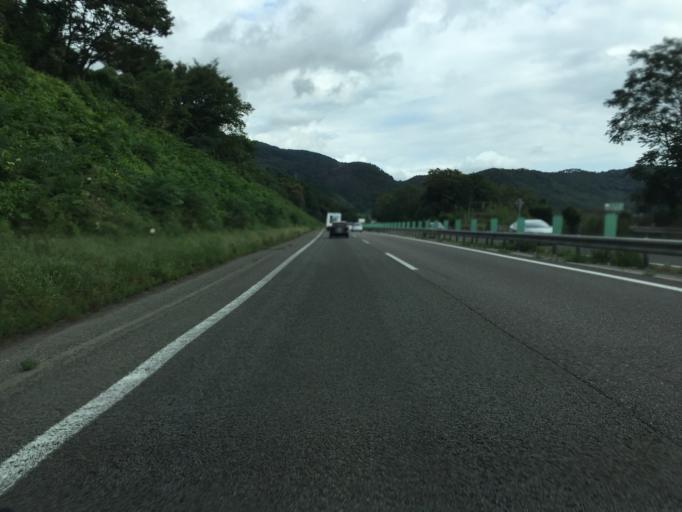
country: JP
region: Fukushima
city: Yanagawamachi-saiwaicho
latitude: 37.8868
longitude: 140.5444
